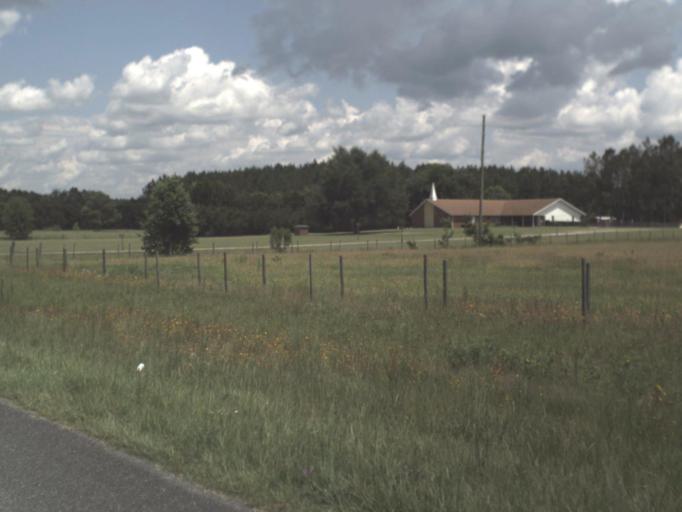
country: US
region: Florida
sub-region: Gilchrist County
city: Trenton
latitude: 29.6131
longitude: -82.8524
